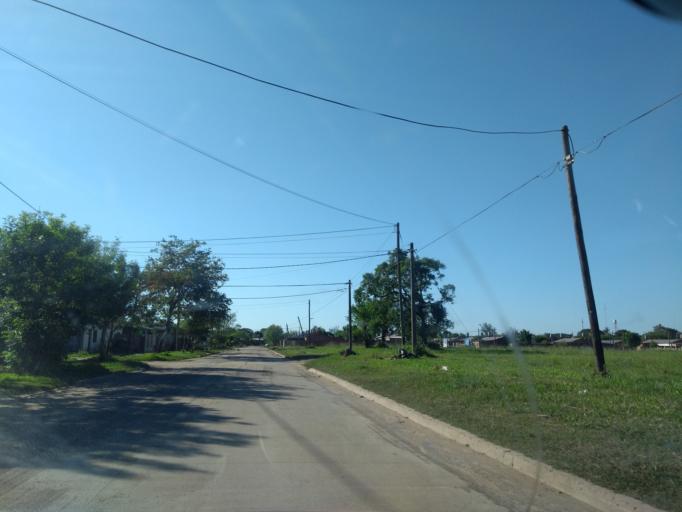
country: AR
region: Chaco
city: Fontana
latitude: -27.4184
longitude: -59.0446
